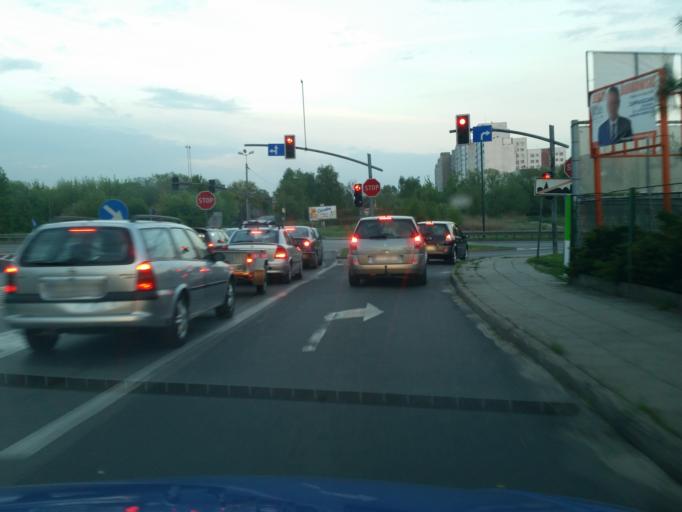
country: PL
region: Silesian Voivodeship
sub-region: Powiat bedzinski
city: Bedzin
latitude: 50.3072
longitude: 19.1799
